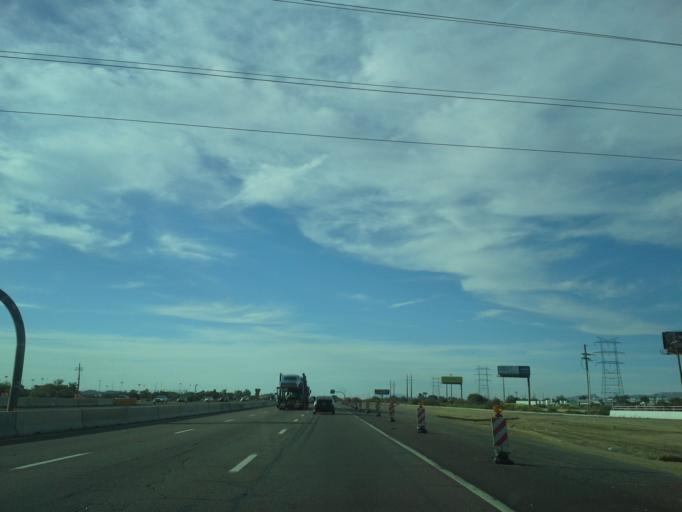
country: US
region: Arizona
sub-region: Pima County
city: Flowing Wells
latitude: 32.3291
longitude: -111.0571
